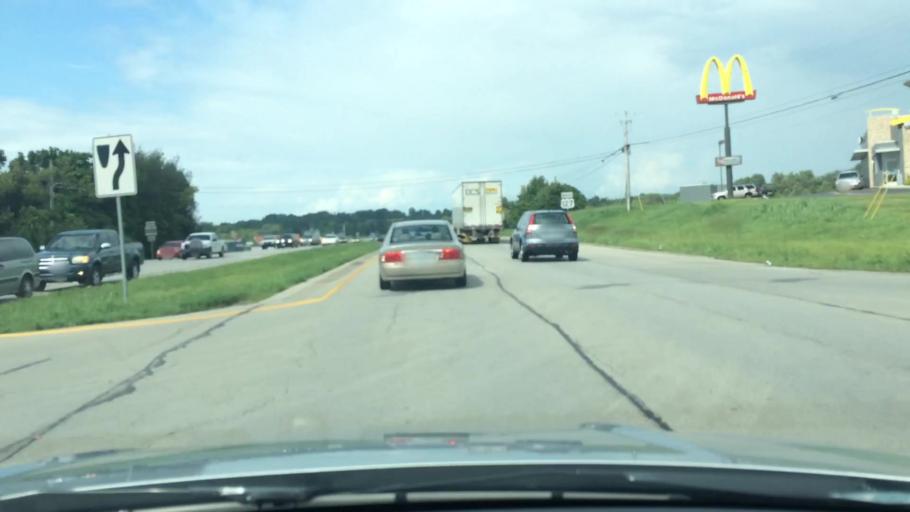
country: US
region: Kentucky
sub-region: Anderson County
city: Lawrenceburg
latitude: 38.0679
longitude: -84.9196
